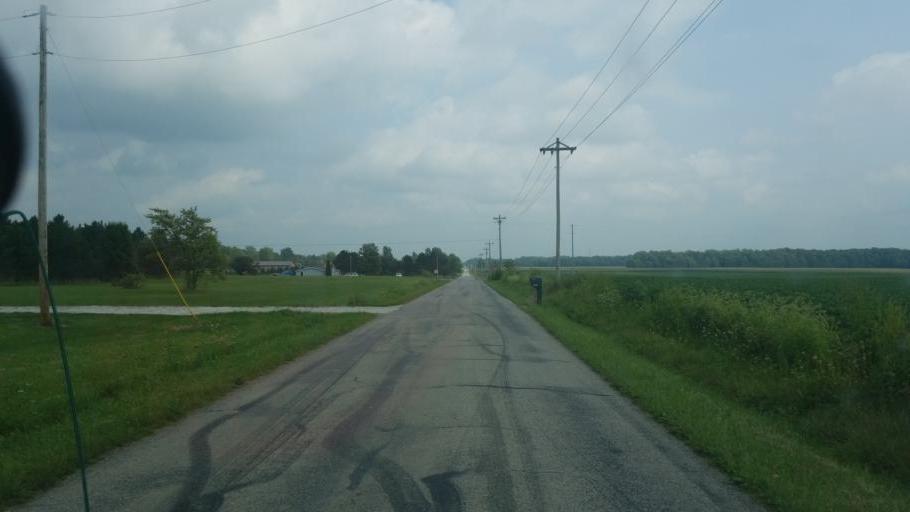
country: US
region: Ohio
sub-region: Huron County
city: Greenwich
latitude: 41.0938
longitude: -82.5148
